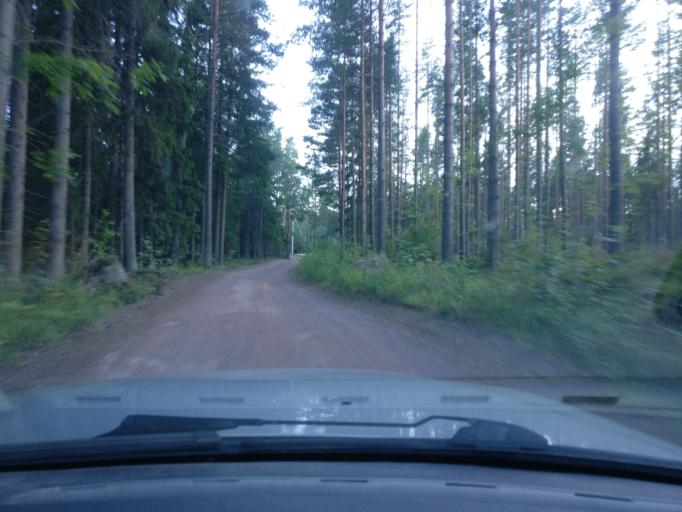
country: FI
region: Kymenlaakso
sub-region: Kotka-Hamina
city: Broby
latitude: 60.4726
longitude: 26.7769
